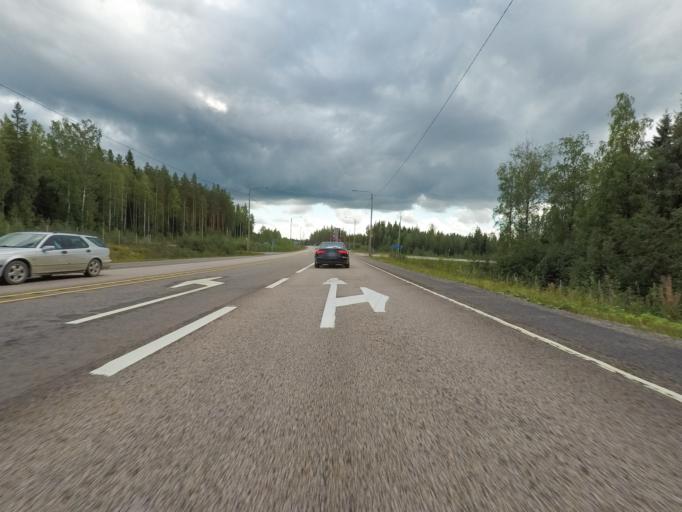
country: FI
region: Central Finland
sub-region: Joutsa
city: Leivonmaeki
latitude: 61.9721
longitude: 26.0719
